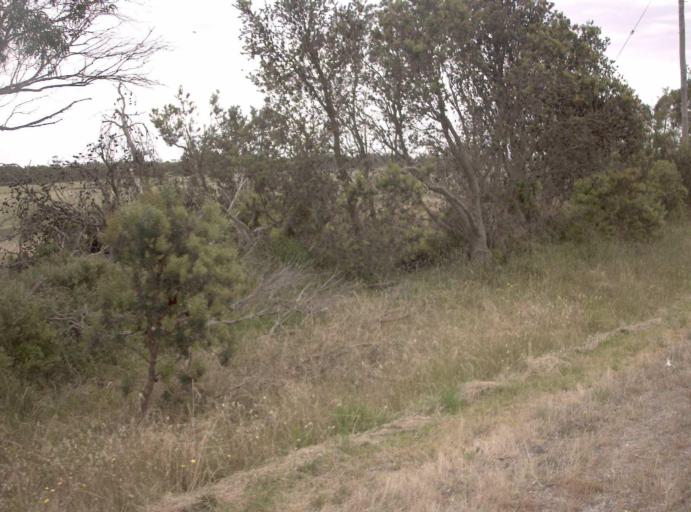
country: AU
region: Victoria
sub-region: Wellington
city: Sale
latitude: -38.1986
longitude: 147.3371
